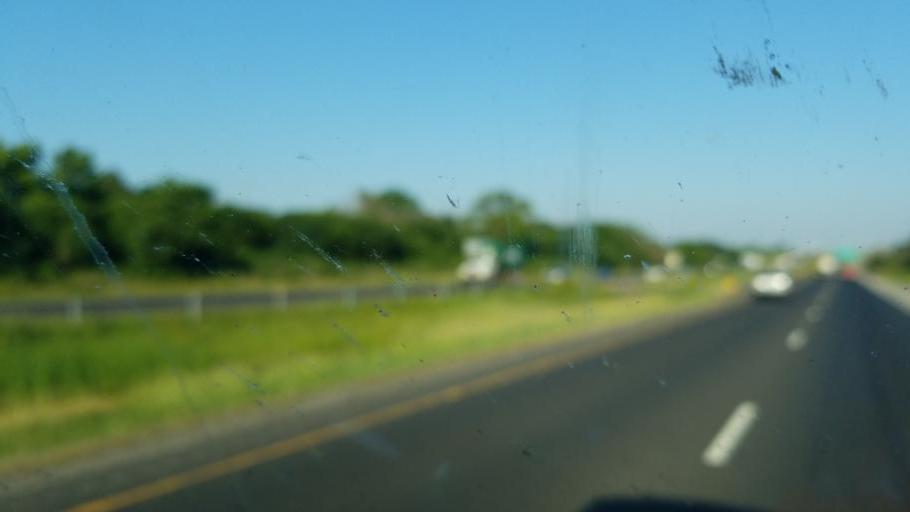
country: US
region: Illinois
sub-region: Will County
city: Shorewood
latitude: 41.4868
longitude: -88.1832
